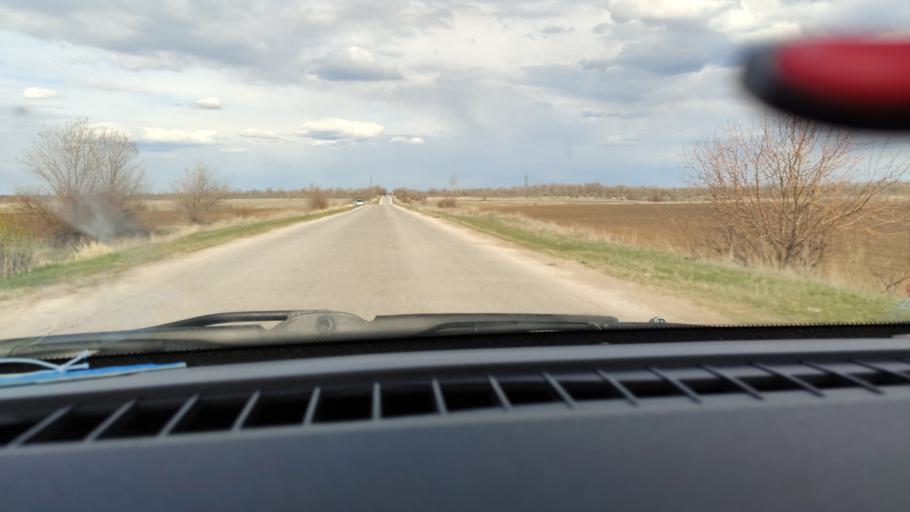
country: RU
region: Saratov
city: Rovnoye
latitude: 50.9407
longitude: 46.1250
